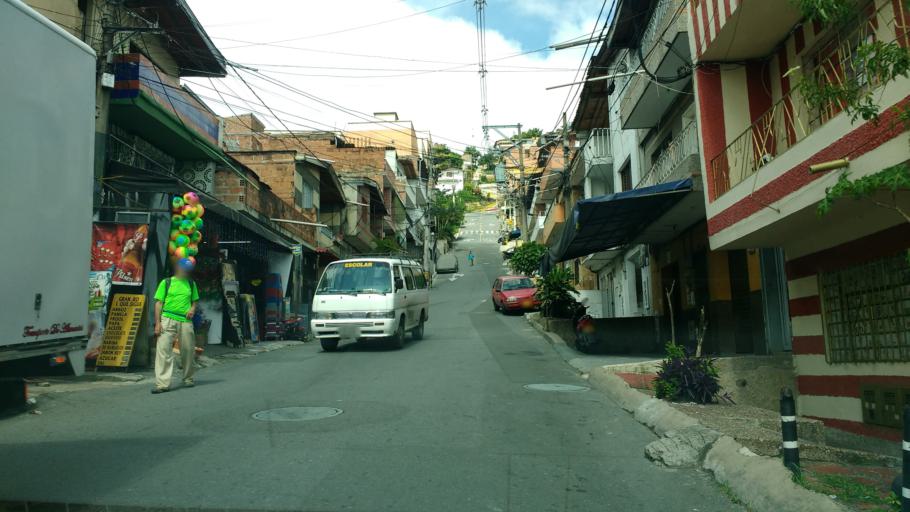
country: CO
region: Antioquia
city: Medellin
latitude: 6.2611
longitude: -75.6094
